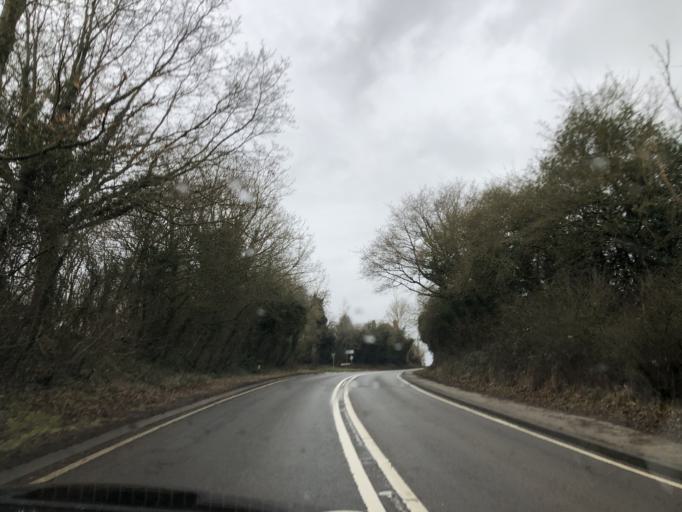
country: GB
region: England
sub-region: Warwickshire
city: Henley in Arden
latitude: 52.2852
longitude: -1.7531
